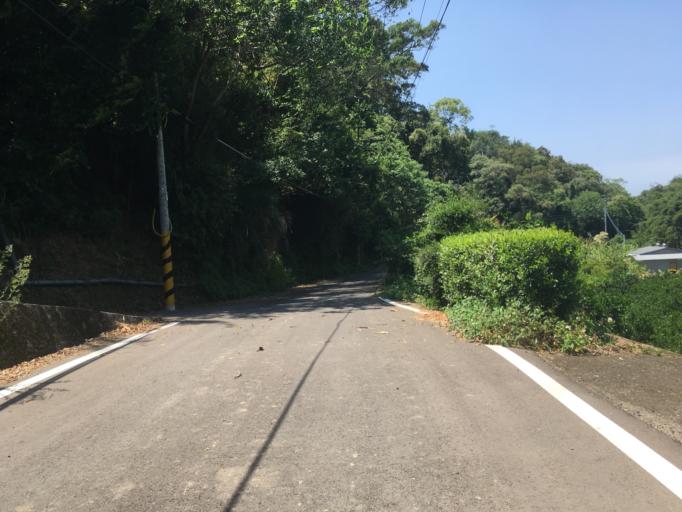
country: TW
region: Taiwan
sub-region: Hsinchu
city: Hsinchu
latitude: 24.7311
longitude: 120.9807
